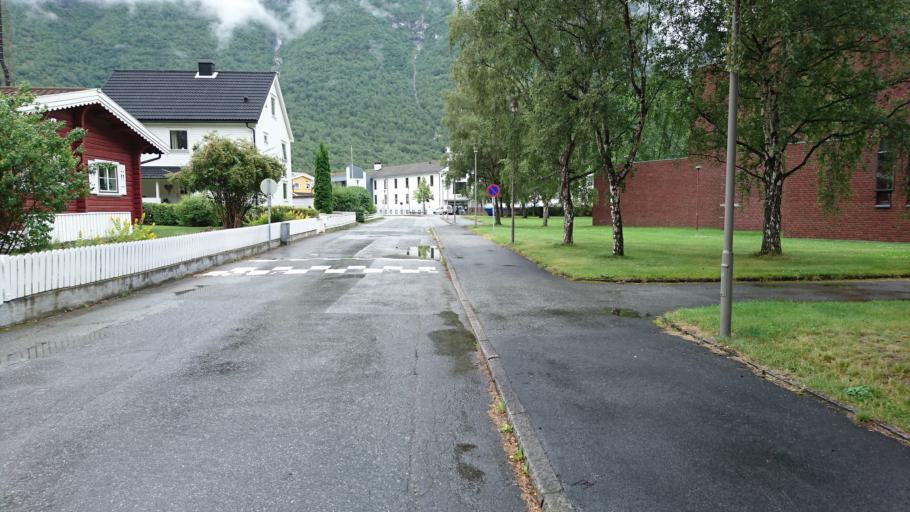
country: NO
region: Sogn og Fjordane
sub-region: Ardal
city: Farnes
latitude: 61.3105
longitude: 7.8019
